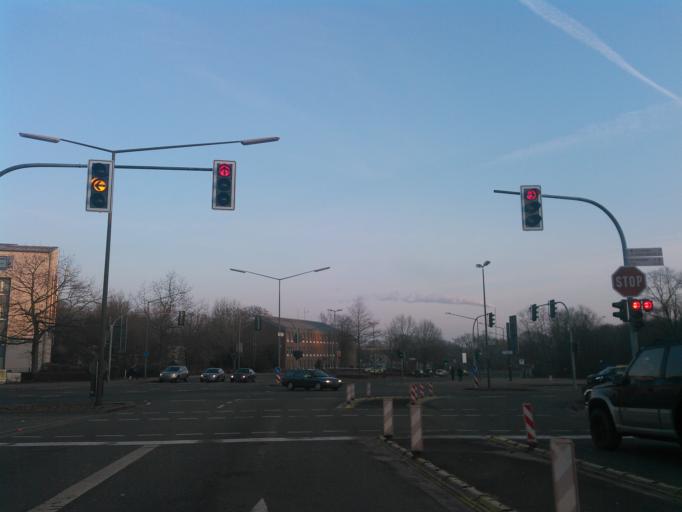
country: DE
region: North Rhine-Westphalia
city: Marl
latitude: 51.6579
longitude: 7.1021
